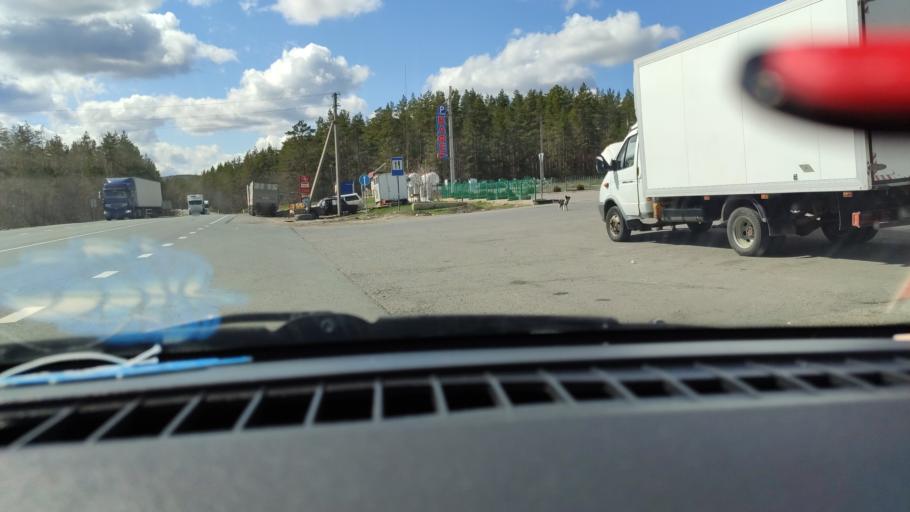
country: RU
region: Saratov
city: Khvalynsk
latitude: 52.5213
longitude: 48.0194
